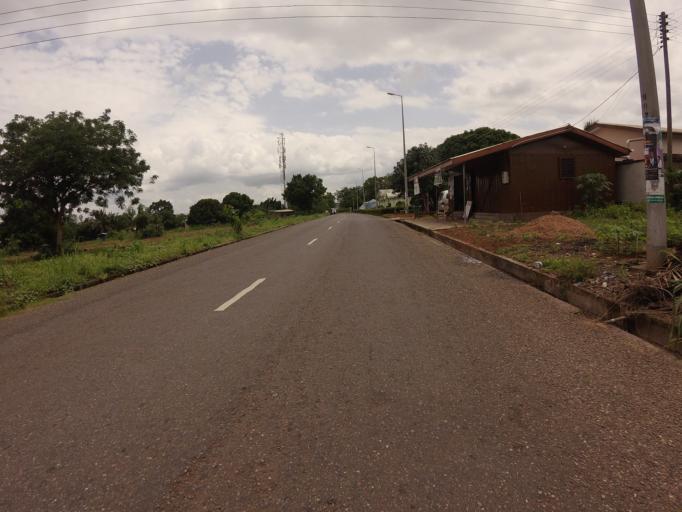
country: GH
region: Volta
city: Ho
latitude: 6.5932
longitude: 0.4651
